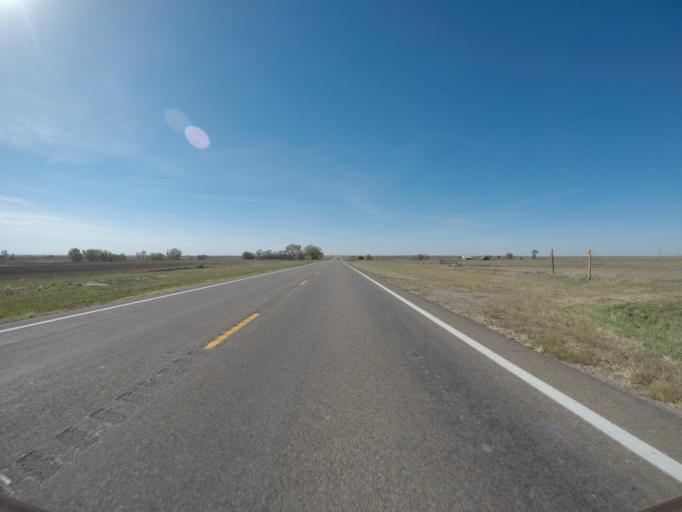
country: US
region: Kansas
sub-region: Smith County
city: Smith Center
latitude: 39.7710
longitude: -98.9399
